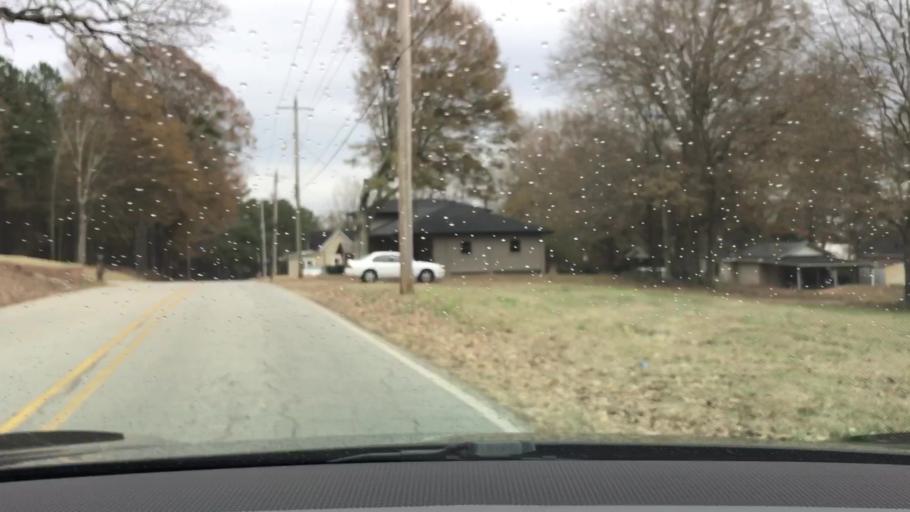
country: US
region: Georgia
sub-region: Gwinnett County
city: Buford
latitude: 34.1126
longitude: -84.0108
